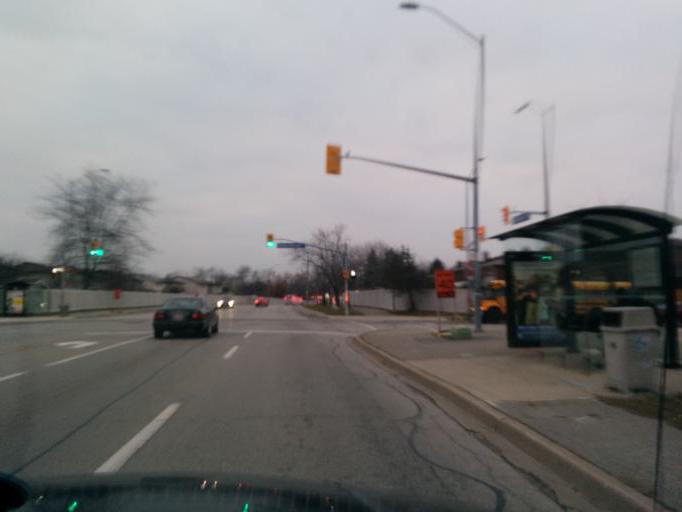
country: CA
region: Ontario
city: Mississauga
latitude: 43.6125
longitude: -79.6201
